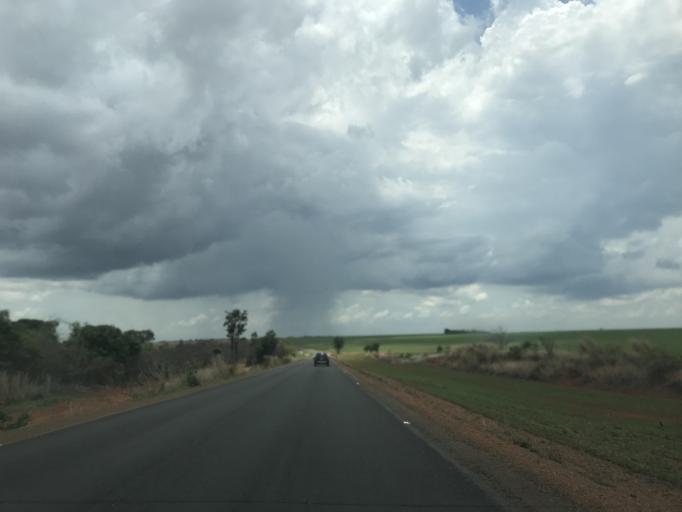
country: BR
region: Goias
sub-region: Vianopolis
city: Vianopolis
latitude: -16.8118
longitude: -48.5206
